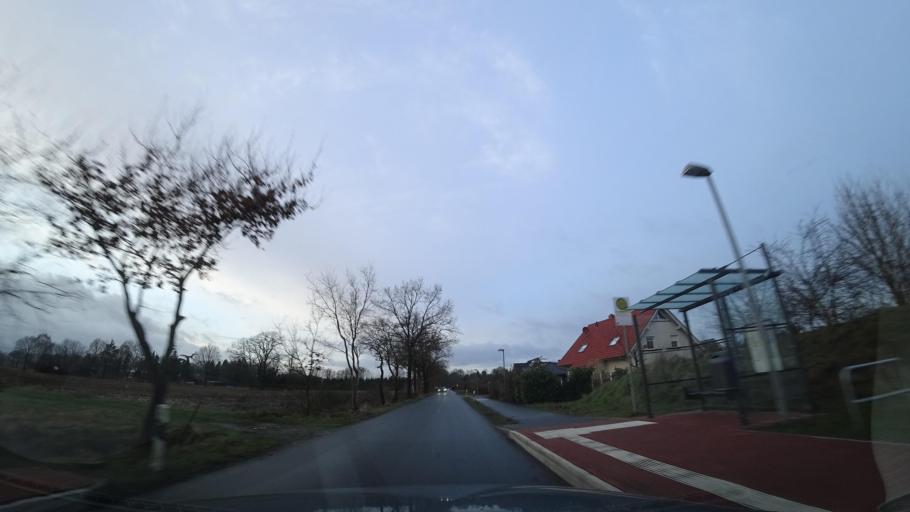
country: DE
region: Lower Saxony
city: Hatten
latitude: 53.0496
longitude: 8.2964
